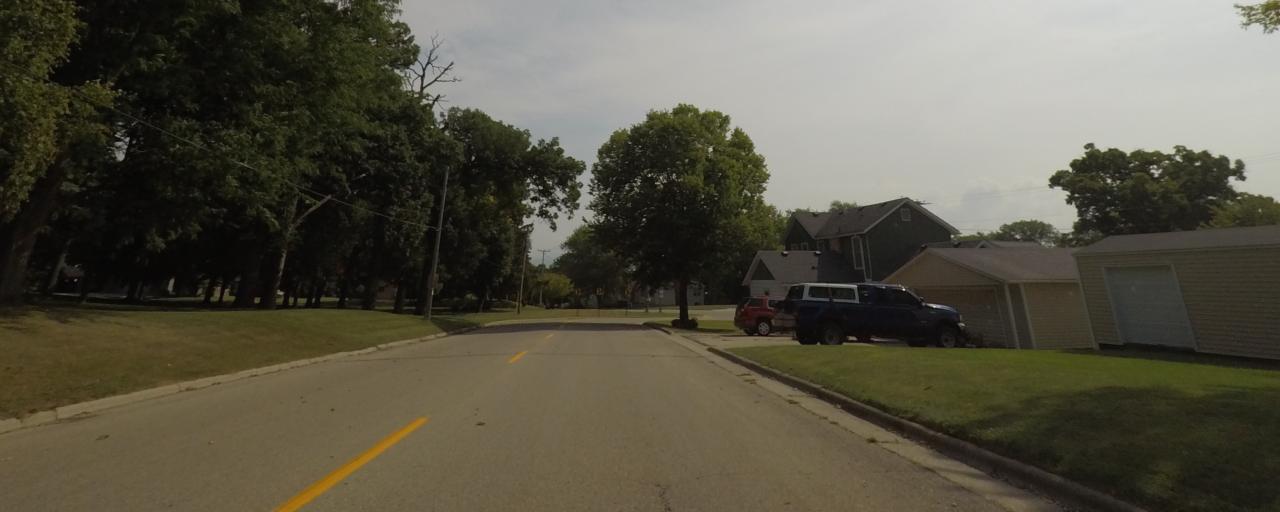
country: US
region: Wisconsin
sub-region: Jefferson County
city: Jefferson
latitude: 42.9969
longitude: -88.8200
